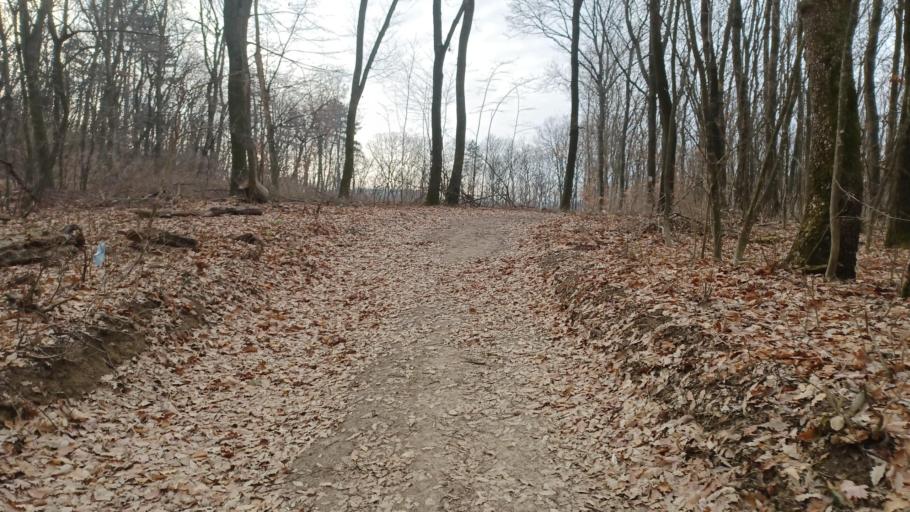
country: HU
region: Tolna
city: Szentgalpuszta
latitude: 46.3364
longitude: 18.6257
